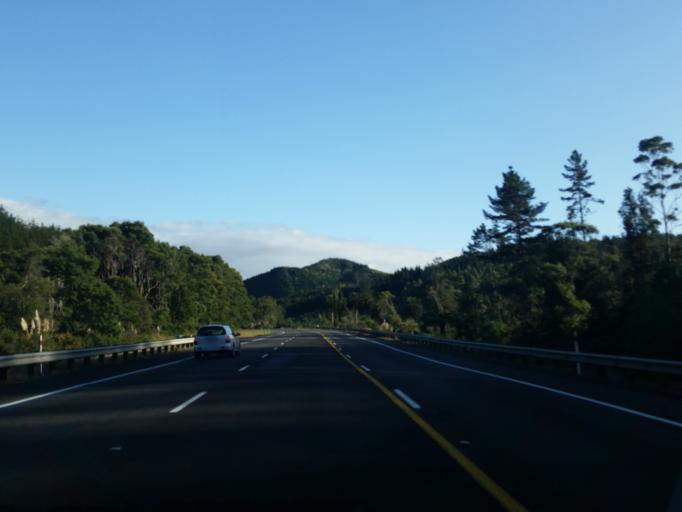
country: NZ
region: Bay of Plenty
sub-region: Western Bay of Plenty District
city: Waihi Beach
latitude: -37.4604
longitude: 175.9099
